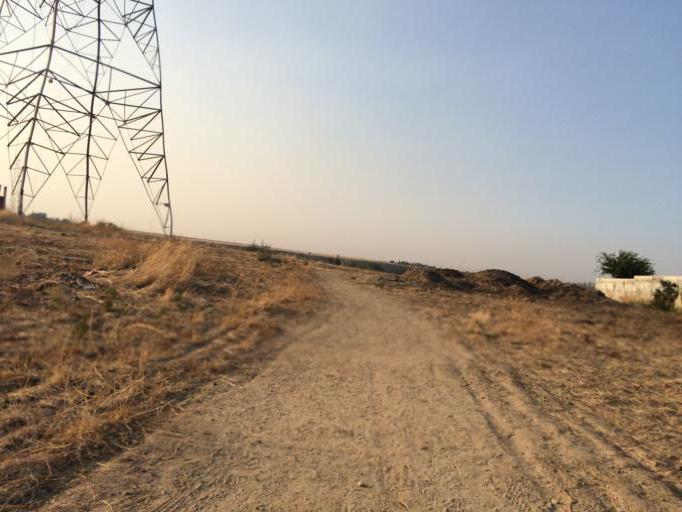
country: US
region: California
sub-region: Fresno County
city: Fresno
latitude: 36.8494
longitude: -119.8107
